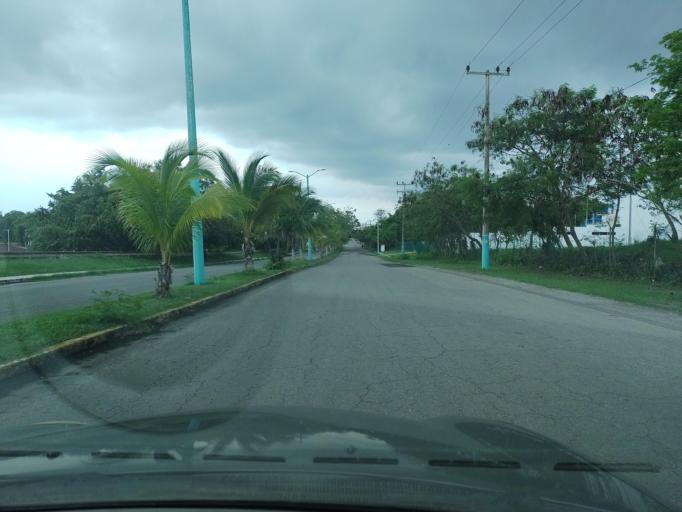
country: MX
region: Quintana Roo
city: Chetumal
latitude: 18.5242
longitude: -88.2733
